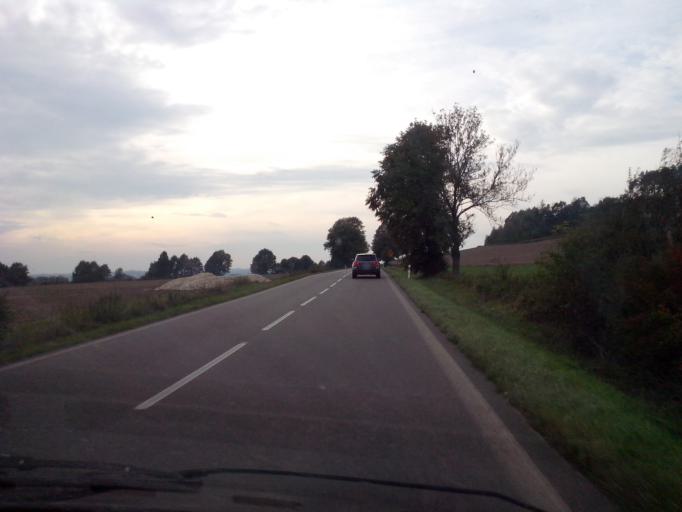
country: PL
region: Subcarpathian Voivodeship
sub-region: Powiat przeworski
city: Jawornik Polski
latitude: 49.8291
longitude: 22.3049
